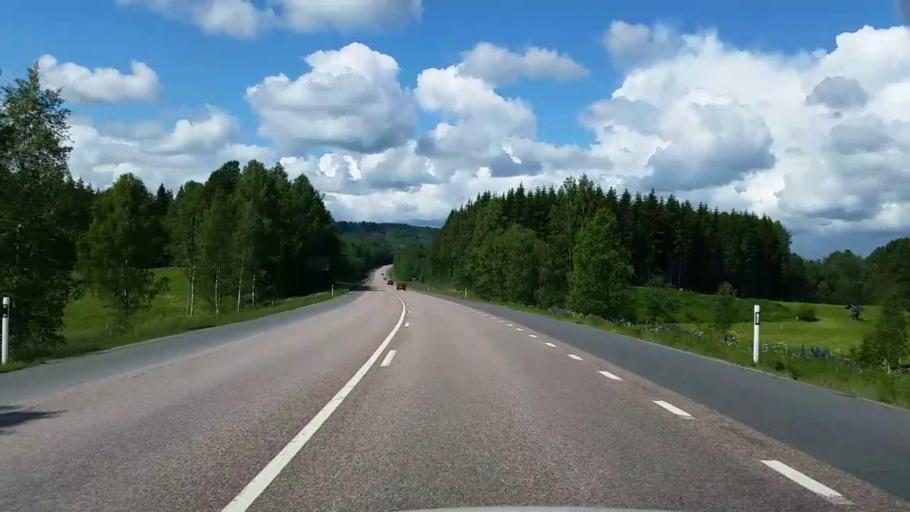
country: SE
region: Vaestmanland
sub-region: Fagersta Kommun
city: Fagersta
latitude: 59.9657
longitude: 15.7595
